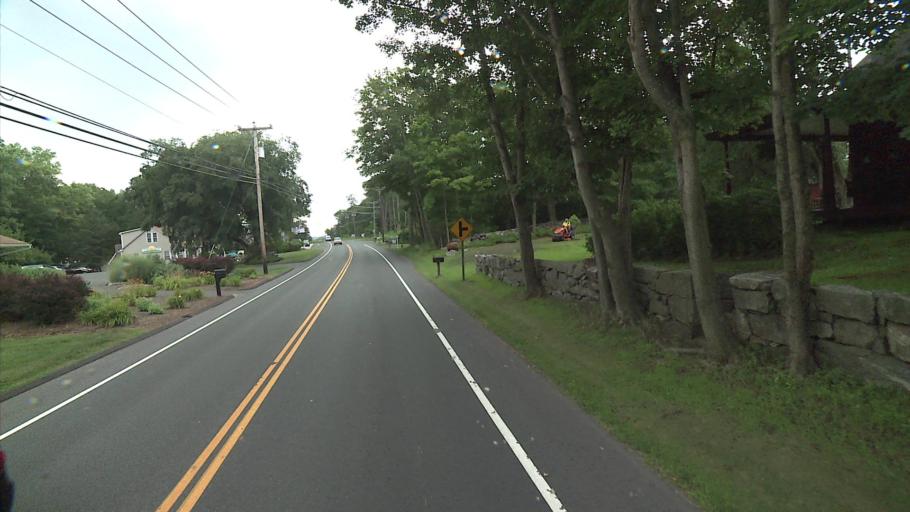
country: US
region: Connecticut
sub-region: New Haven County
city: Southbury
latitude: 41.4666
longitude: -73.1702
